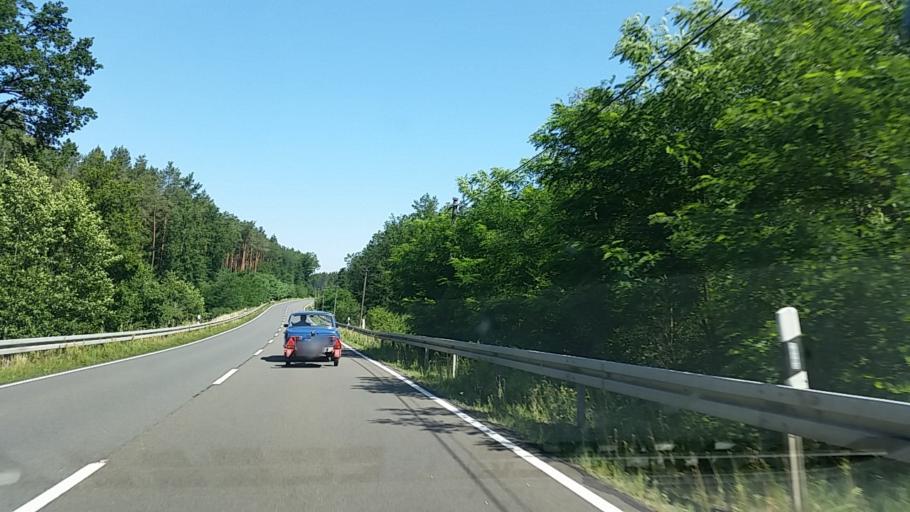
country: DE
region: Saxony-Anhalt
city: Kemberg
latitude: 51.7095
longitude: 12.6189
